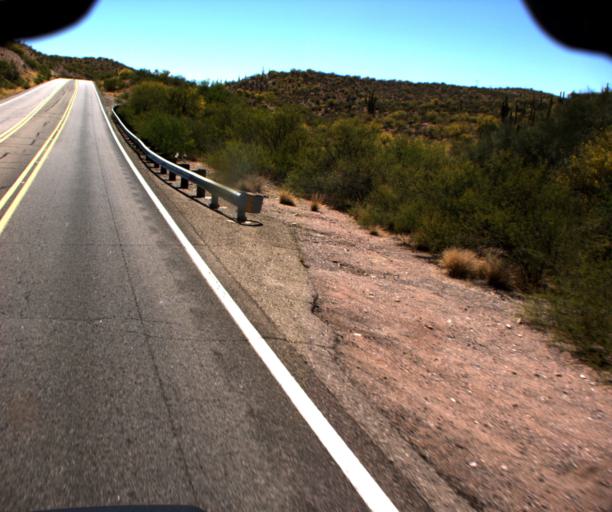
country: US
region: Arizona
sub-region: Pinal County
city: Mammoth
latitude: 32.6734
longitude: -110.6620
